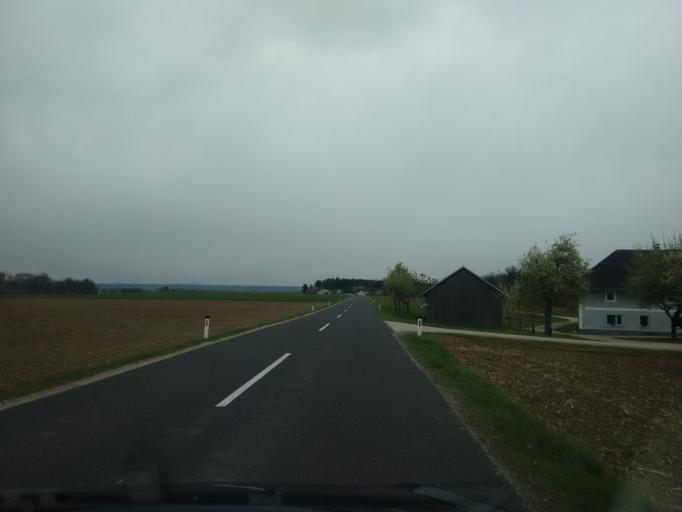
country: AT
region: Upper Austria
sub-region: Wels-Land
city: Holzhausen
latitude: 48.2258
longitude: 14.0719
